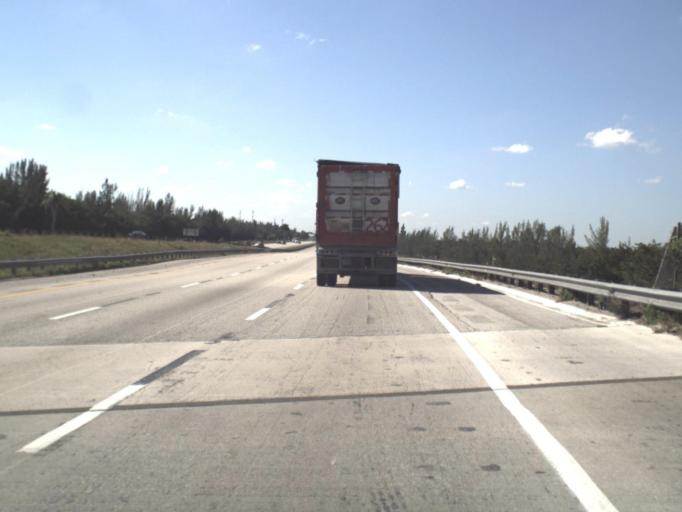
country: US
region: Florida
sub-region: Miami-Dade County
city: Palm Springs North
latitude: 25.9278
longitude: -80.3756
